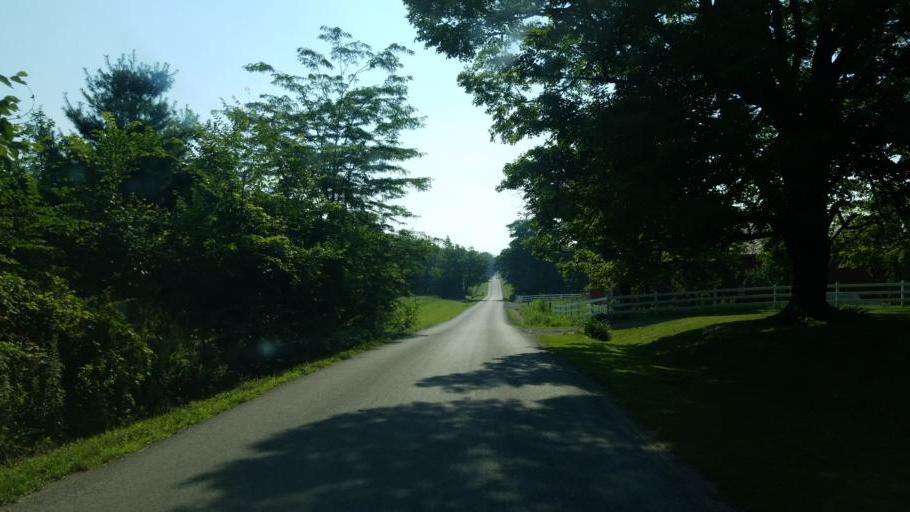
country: US
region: Ohio
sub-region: Knox County
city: Fredericktown
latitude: 40.5352
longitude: -82.6543
